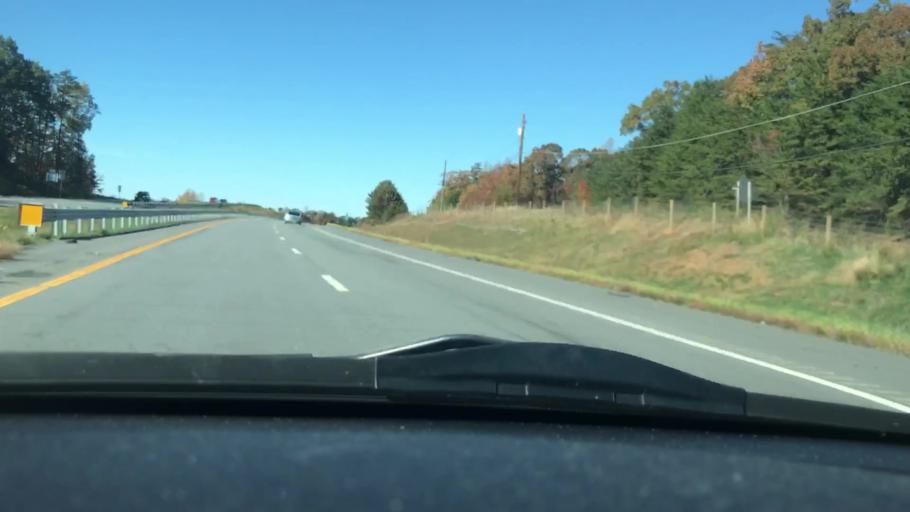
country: US
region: North Carolina
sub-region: Guilford County
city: Stokesdale
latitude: 36.2809
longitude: -79.9380
